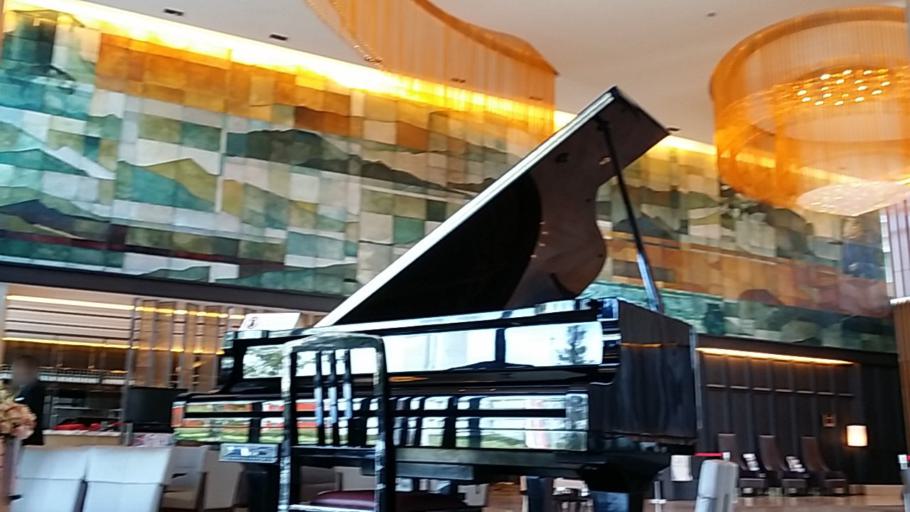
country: TW
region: Taipei
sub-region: Taipei
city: Banqiao
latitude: 25.1820
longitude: 121.4160
